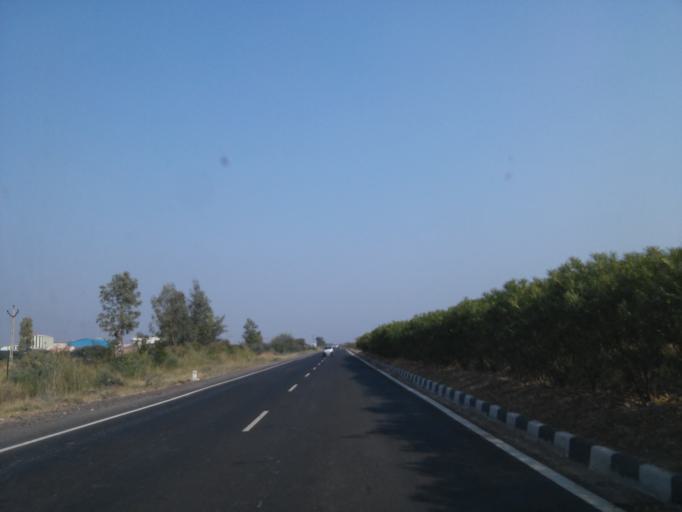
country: IN
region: Gujarat
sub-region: Surendranagar
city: Halvad
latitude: 23.0050
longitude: 71.1379
